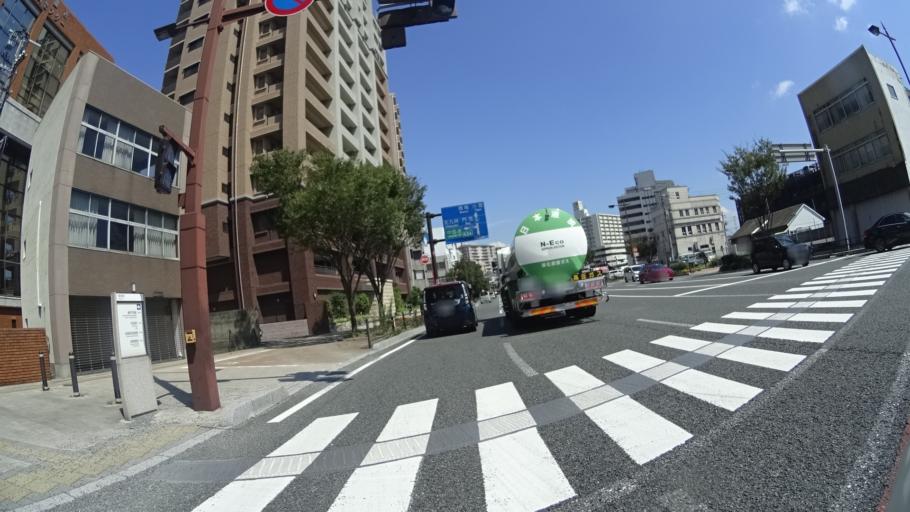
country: JP
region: Yamaguchi
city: Shimonoseki
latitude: 33.9554
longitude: 130.9408
